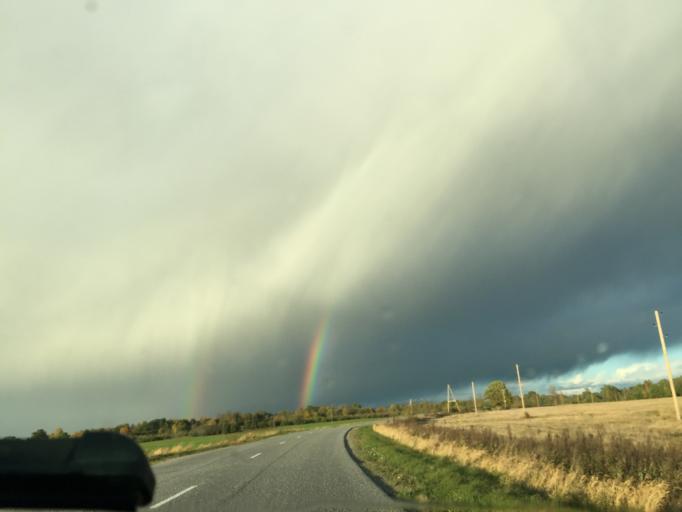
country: LV
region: Broceni
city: Broceni
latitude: 56.8448
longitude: 22.3803
